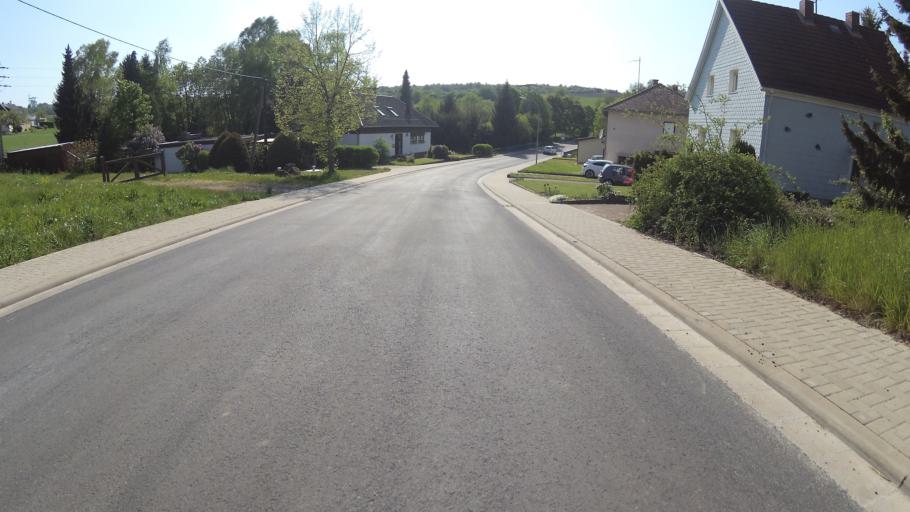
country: DE
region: Saarland
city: Merchweiler
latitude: 49.3587
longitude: 7.0472
